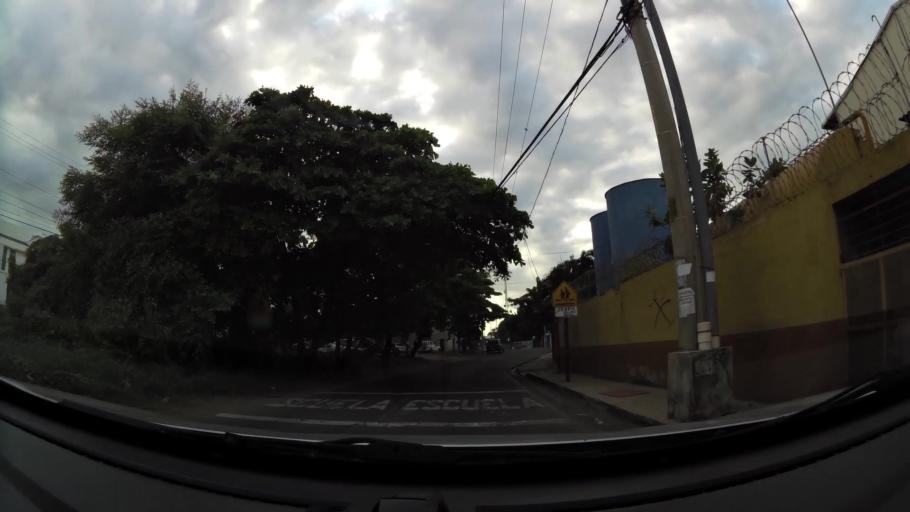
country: CR
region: Puntarenas
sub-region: Canton Central de Puntarenas
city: Puntarenas
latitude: 9.9812
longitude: -84.8094
